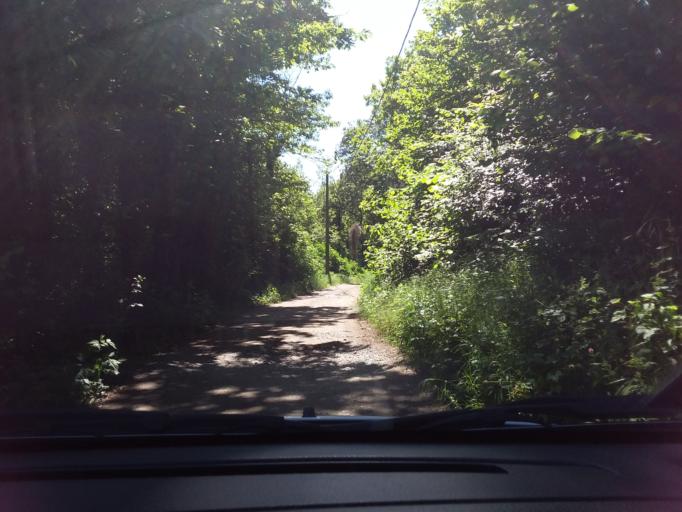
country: IT
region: Piedmont
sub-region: Provincia di Torino
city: Villarbasse
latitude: 45.0585
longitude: 7.4889
